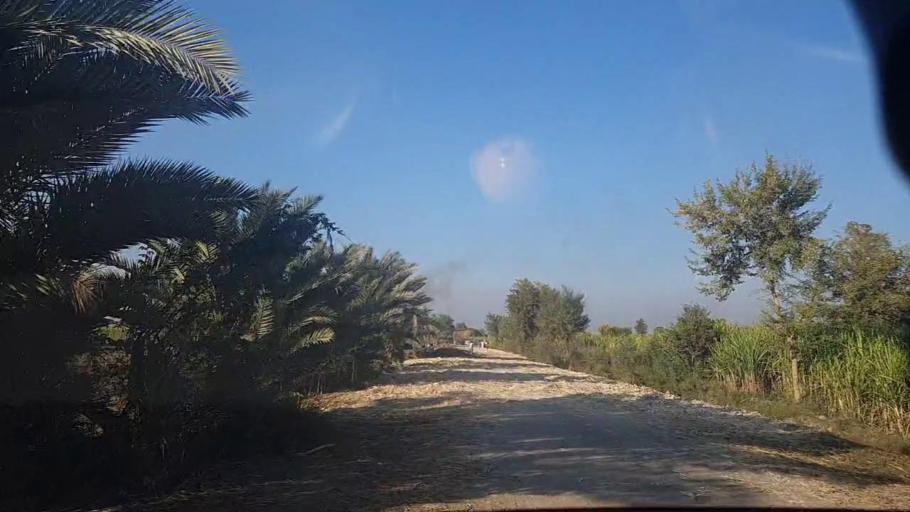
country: PK
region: Sindh
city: Sobhadero
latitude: 27.4209
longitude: 68.4234
